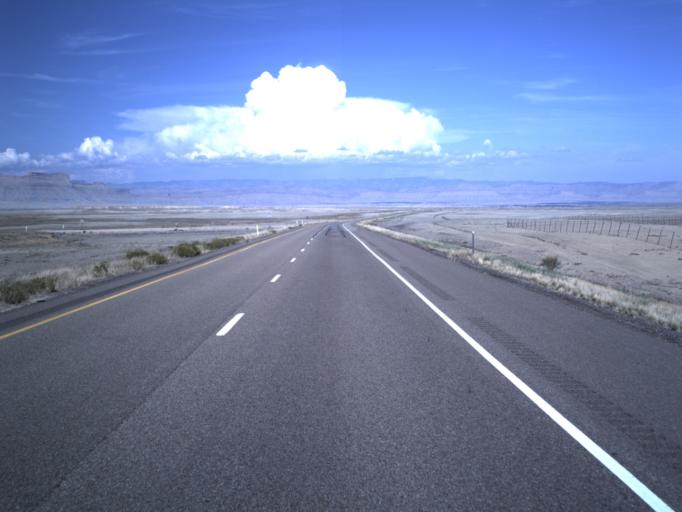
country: US
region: Utah
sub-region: Carbon County
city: East Carbon City
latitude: 38.9466
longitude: -110.3231
